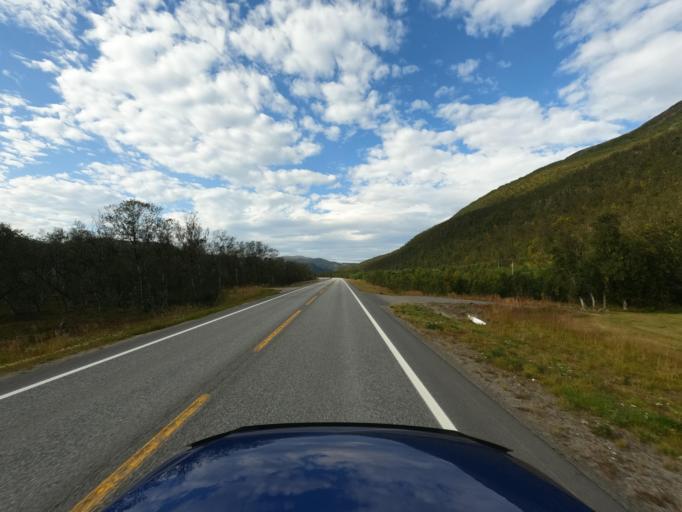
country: NO
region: Finnmark Fylke
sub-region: Kvalsund
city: Kvalsund
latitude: 70.4484
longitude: 24.3709
